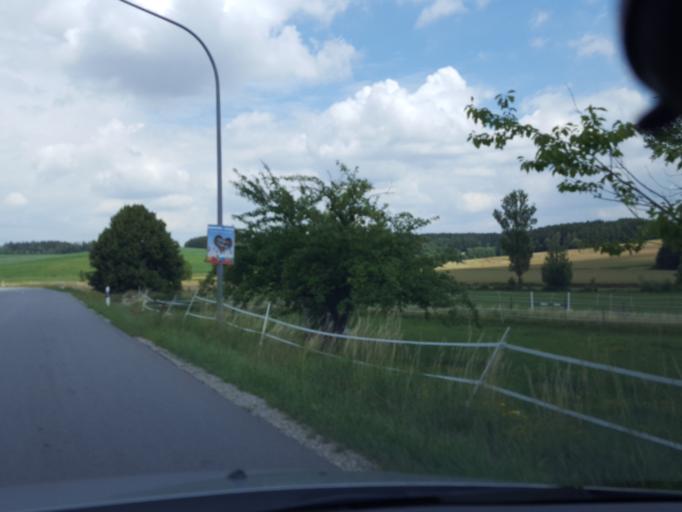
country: DE
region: Bavaria
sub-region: Upper Bavaria
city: Egglkofen
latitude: 48.4308
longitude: 12.4216
